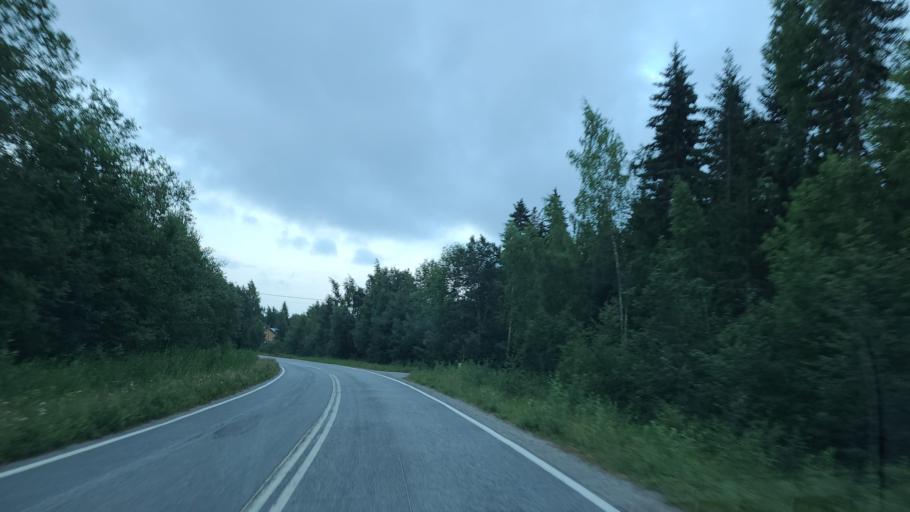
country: FI
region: Ostrobothnia
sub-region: Vaasa
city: Replot
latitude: 63.2743
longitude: 21.1398
